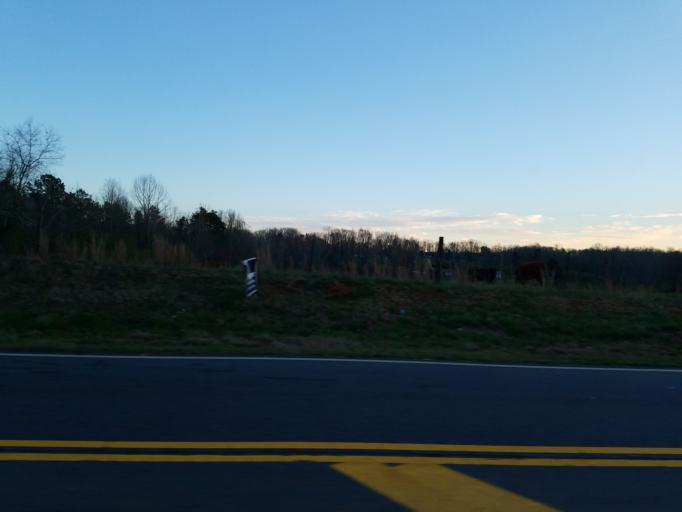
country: US
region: Georgia
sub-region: Hall County
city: Flowery Branch
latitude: 34.2909
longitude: -84.0210
